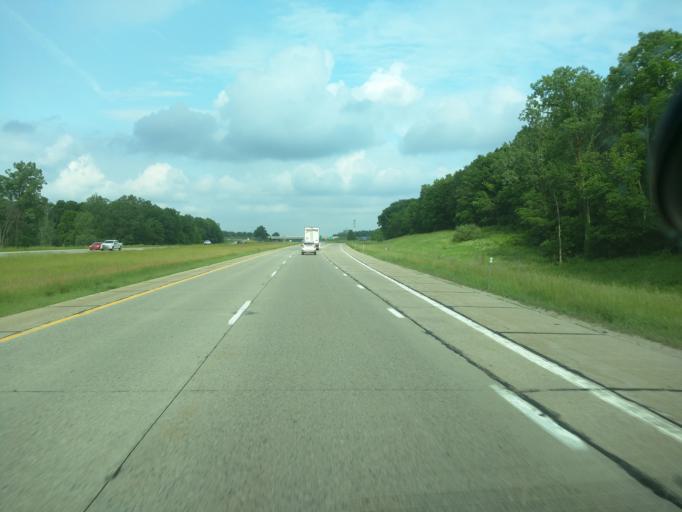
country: US
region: Michigan
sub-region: Clinton County
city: DeWitt
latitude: 42.8174
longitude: -84.5519
